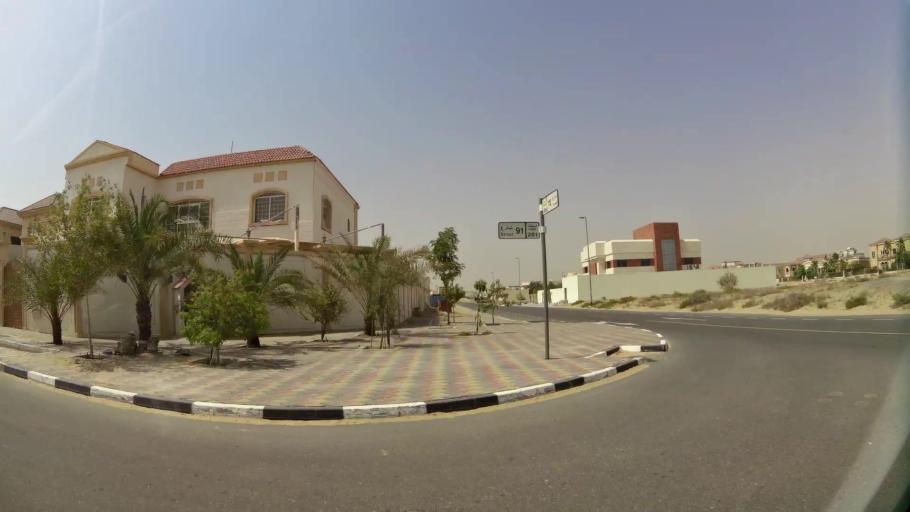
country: AE
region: Ash Shariqah
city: Sharjah
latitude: 25.2483
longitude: 55.4887
